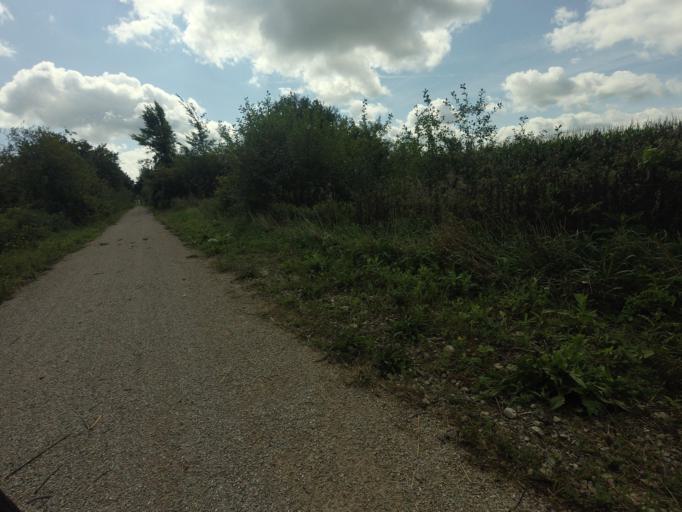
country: CA
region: Ontario
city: Huron East
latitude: 43.6558
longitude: -81.2403
